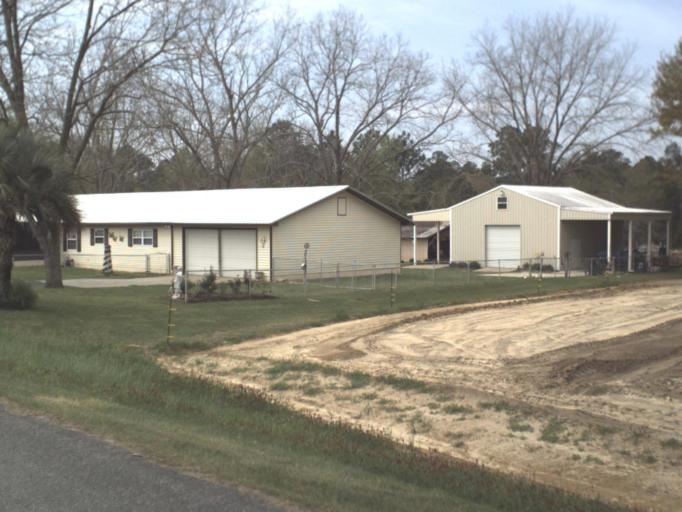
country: US
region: Florida
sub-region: Holmes County
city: Bonifay
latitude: 30.8243
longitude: -85.6686
